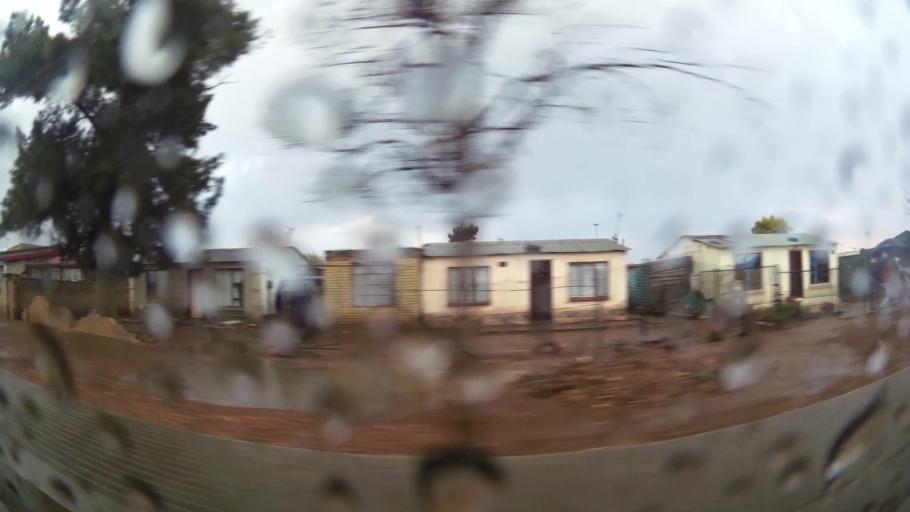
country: ZA
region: Gauteng
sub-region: Ekurhuleni Metropolitan Municipality
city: Germiston
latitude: -26.3518
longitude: 28.1410
